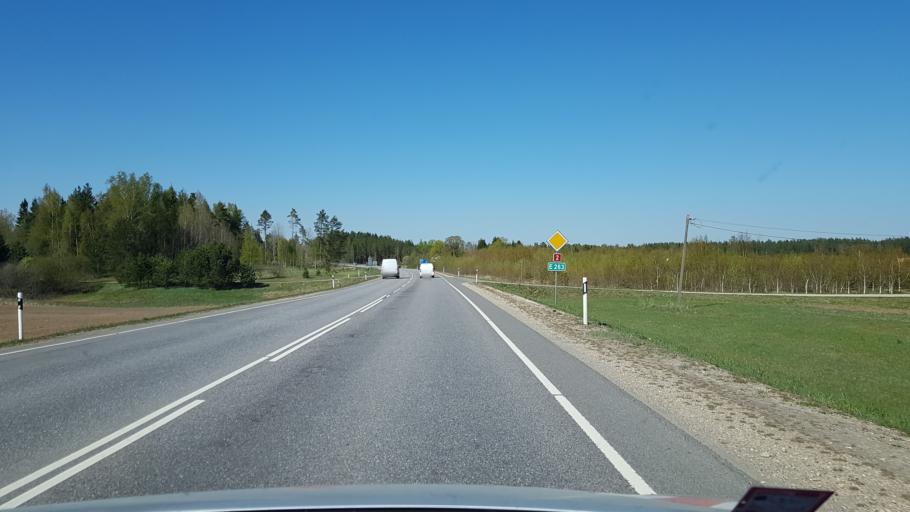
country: EE
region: Tartu
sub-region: UElenurme vald
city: Ulenurme
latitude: 58.0742
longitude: 26.7347
